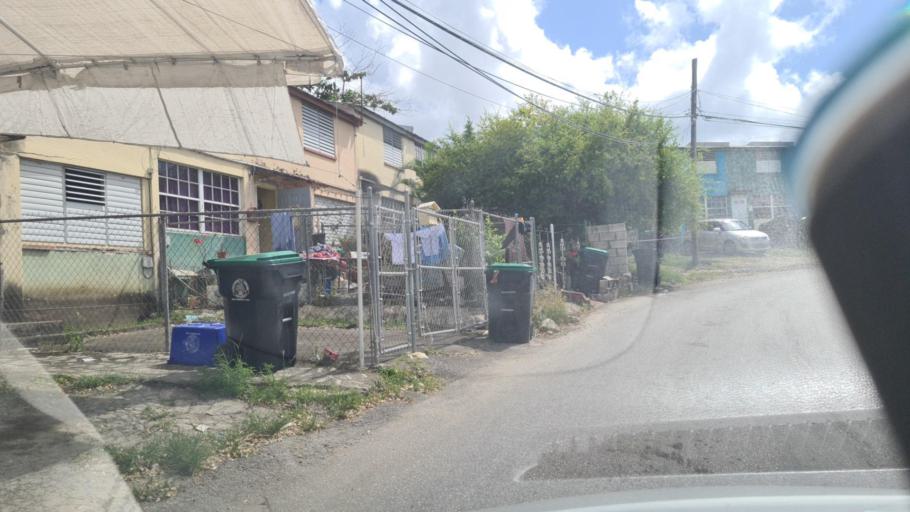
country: BB
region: Saint Michael
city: Bridgetown
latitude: 13.0993
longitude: -59.5827
